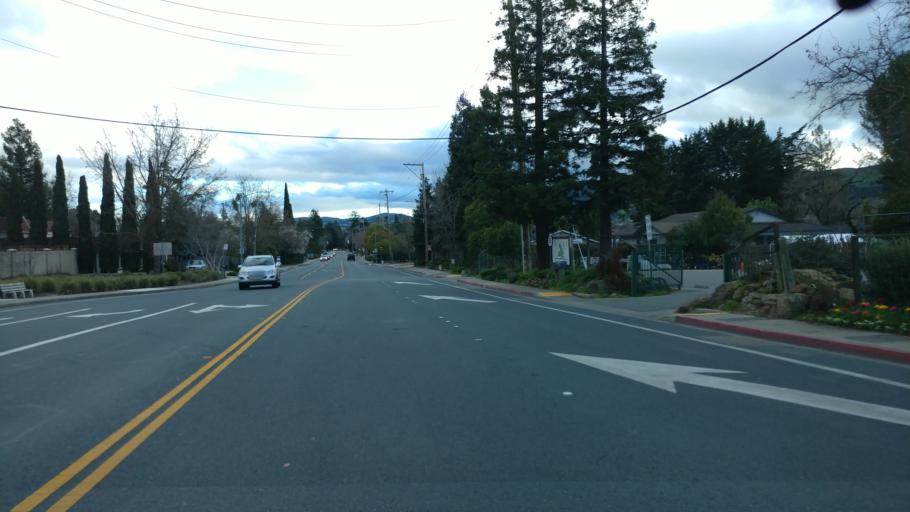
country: US
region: California
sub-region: Contra Costa County
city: Danville
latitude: 37.8303
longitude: -121.9873
